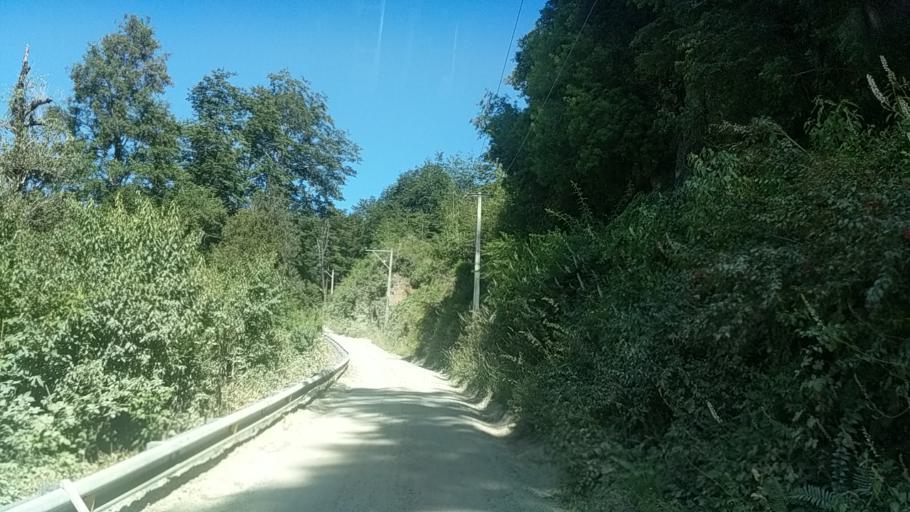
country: CL
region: Araucania
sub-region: Provincia de Cautin
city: Pucon
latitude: -39.0637
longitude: -71.7281
